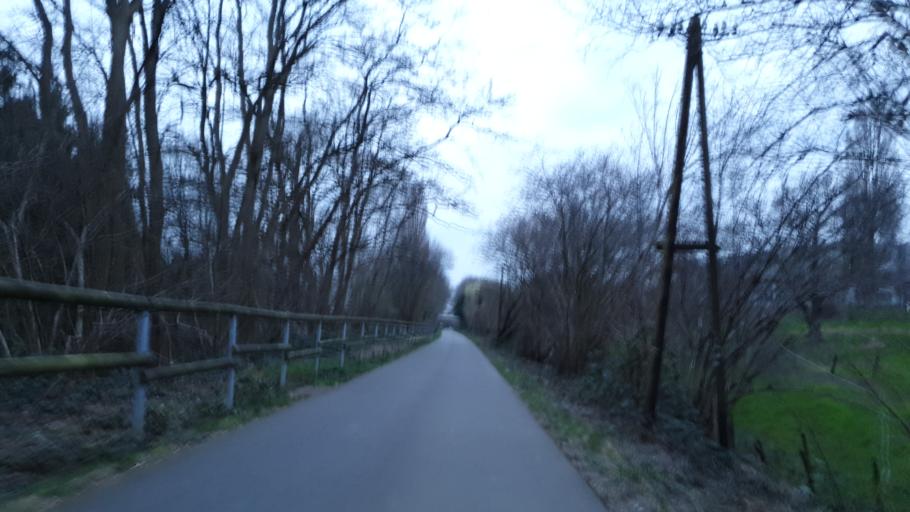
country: DE
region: North Rhine-Westphalia
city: Burscheid
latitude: 51.0856
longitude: 7.0938
